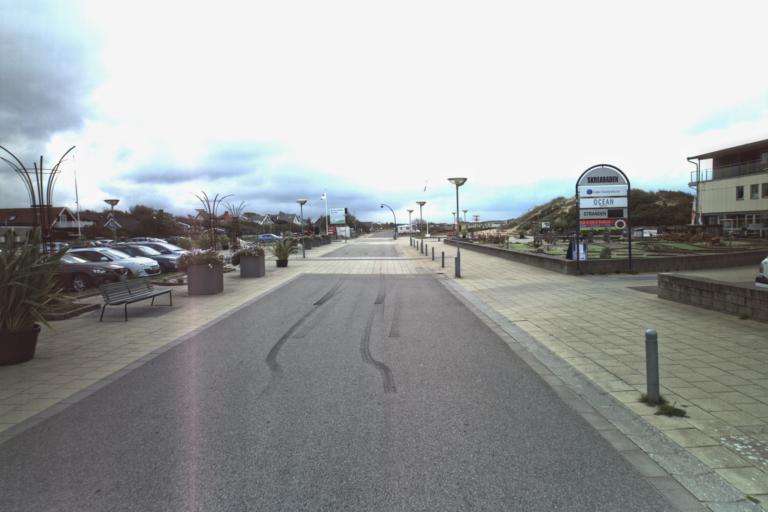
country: SE
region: Halland
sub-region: Falkenbergs Kommun
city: Falkenberg
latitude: 56.8847
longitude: 12.5041
